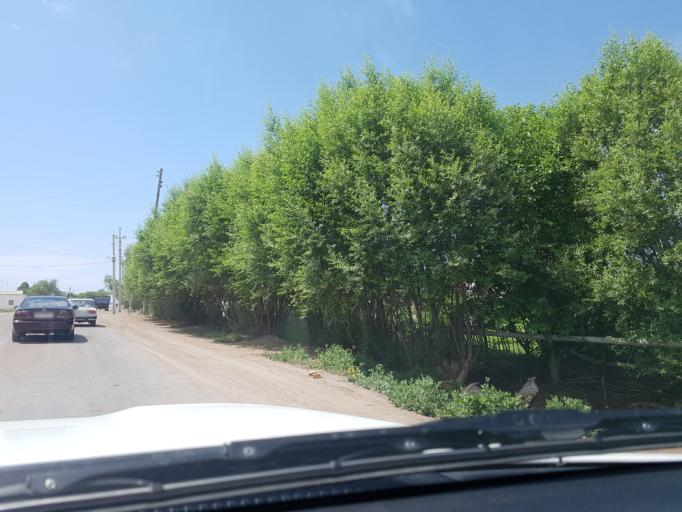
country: TM
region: Dasoguz
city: Koeneuergench
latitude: 42.3163
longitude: 59.1393
